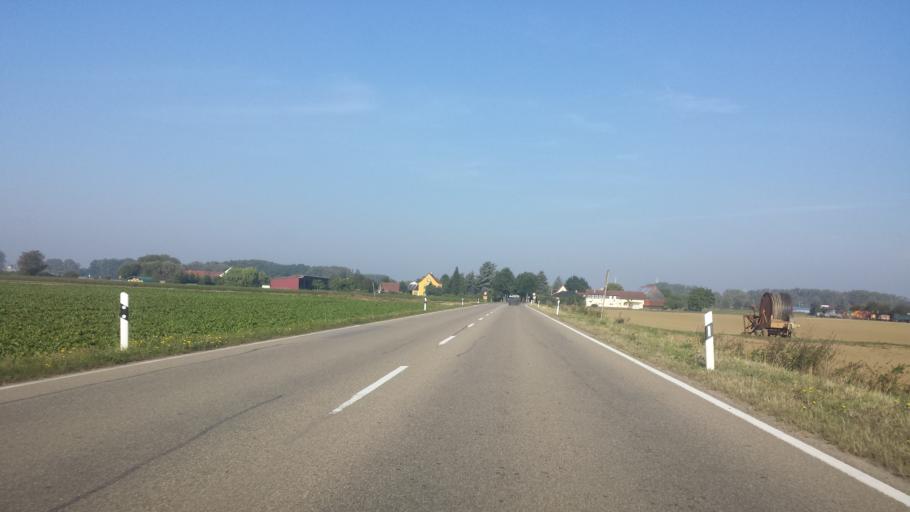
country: DE
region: Rheinland-Pfalz
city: Worms
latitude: 49.6311
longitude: 8.4057
